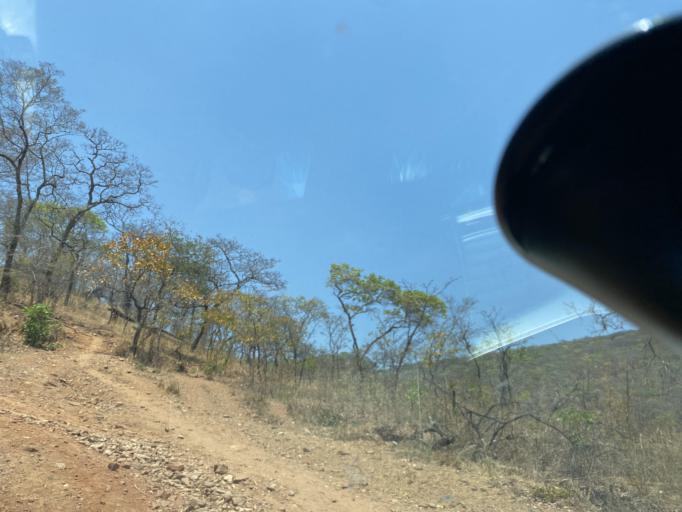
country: ZM
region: Lusaka
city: Kafue
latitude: -15.8081
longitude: 28.4365
